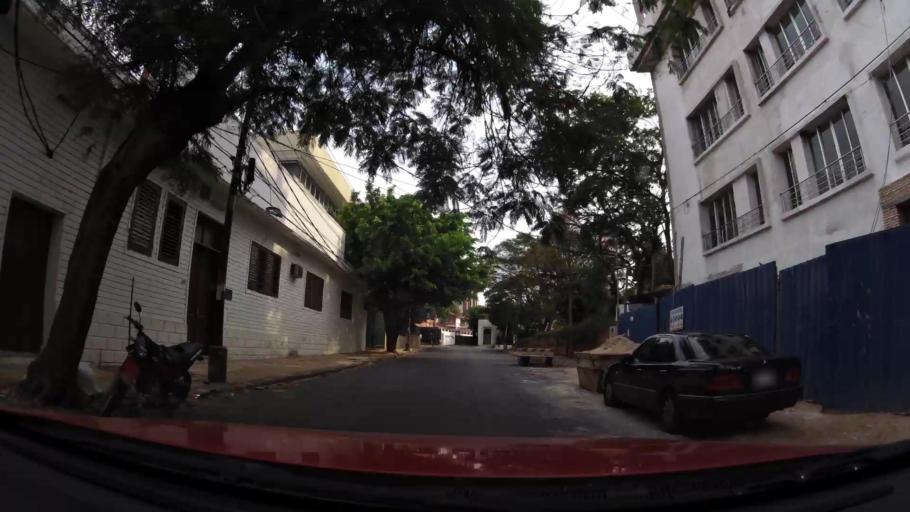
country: PY
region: Asuncion
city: Asuncion
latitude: -25.2890
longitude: -57.6135
